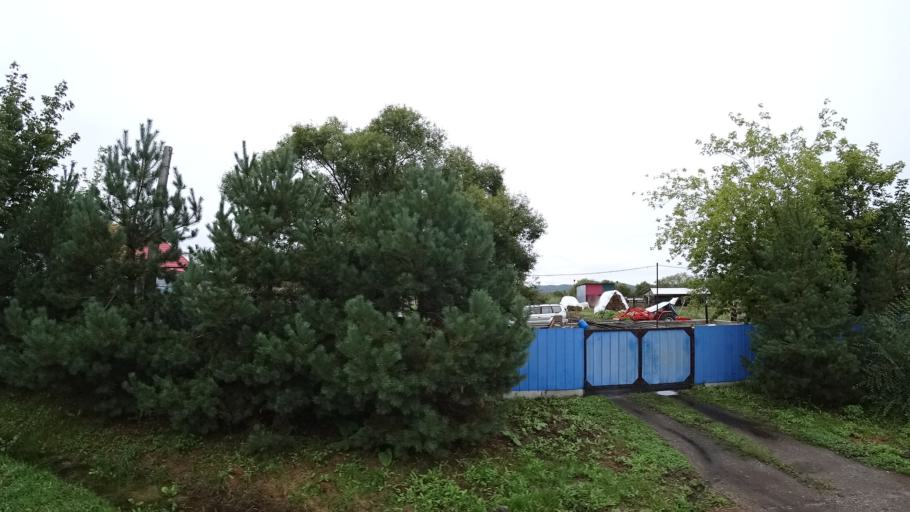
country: RU
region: Primorskiy
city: Monastyrishche
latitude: 44.2122
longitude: 132.4297
